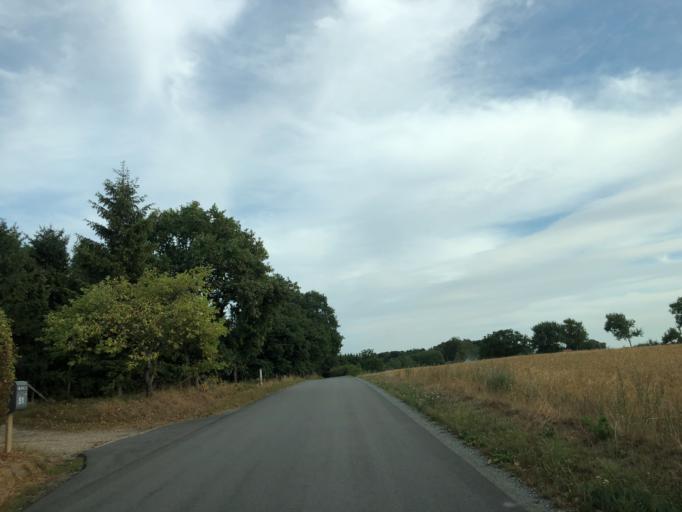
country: DK
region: South Denmark
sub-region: Vejle Kommune
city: Egtved
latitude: 55.6829
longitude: 9.2649
